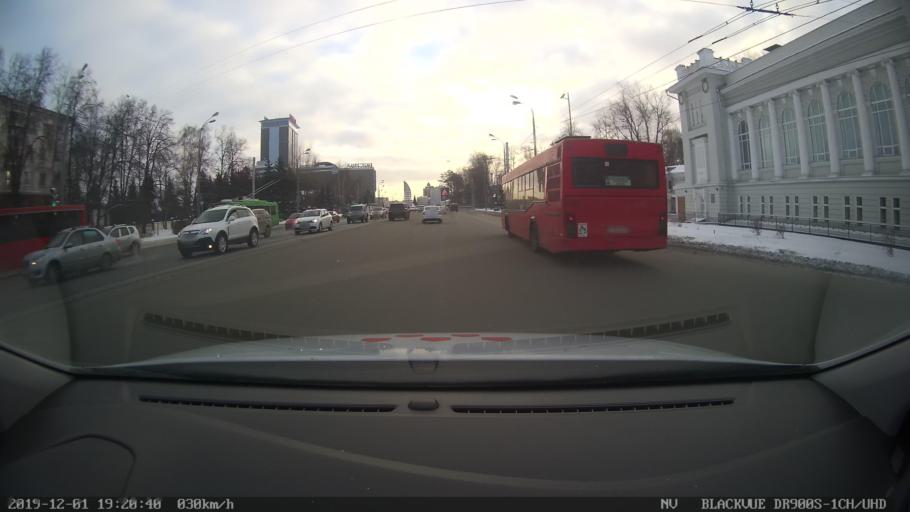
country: RU
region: Tatarstan
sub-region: Gorod Kazan'
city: Kazan
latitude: 55.7958
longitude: 49.1427
